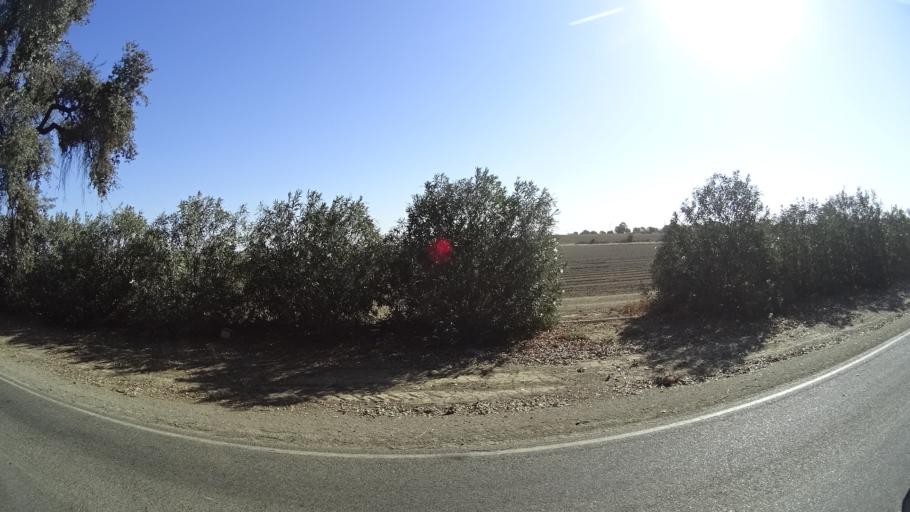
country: US
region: California
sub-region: Yolo County
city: Woodland
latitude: 38.6807
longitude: -121.8679
